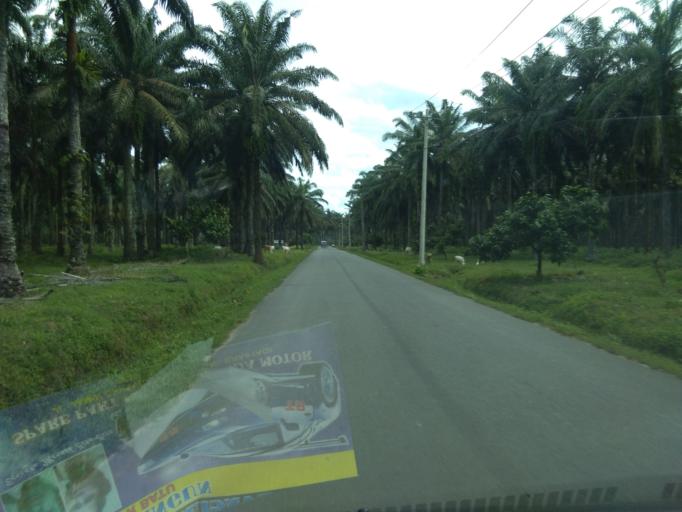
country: ID
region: North Sumatra
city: Deli Tua
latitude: 3.2973
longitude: 98.8077
